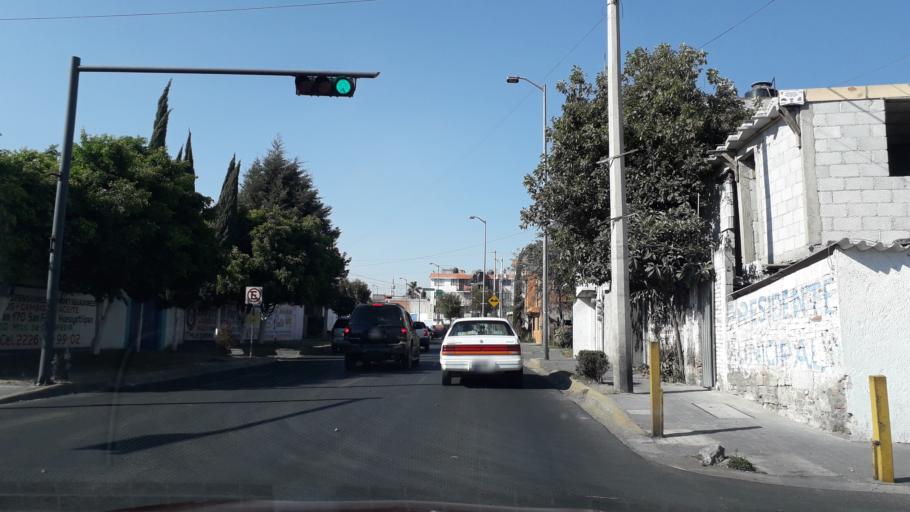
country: MX
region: Puebla
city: Puebla
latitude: 19.0723
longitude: -98.1906
